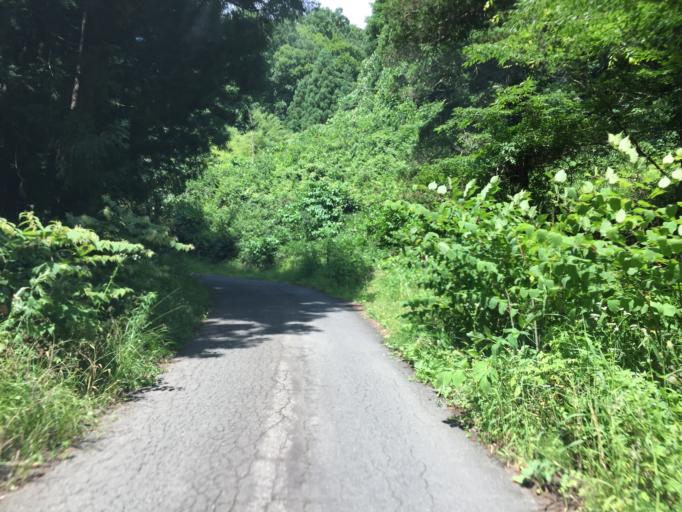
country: JP
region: Fukushima
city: Yanagawamachi-saiwaicho
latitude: 37.7714
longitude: 140.6539
